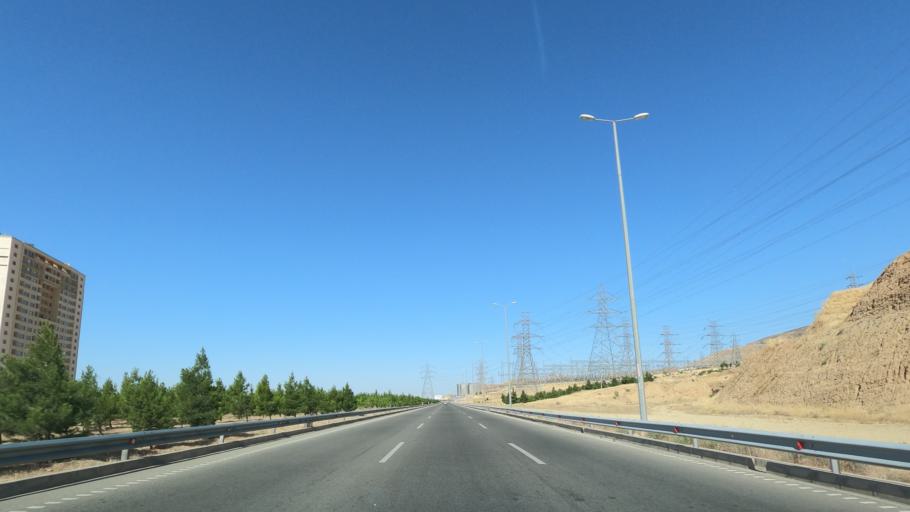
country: IR
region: Tehran
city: Shahr-e Qods
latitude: 35.7551
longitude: 51.1329
